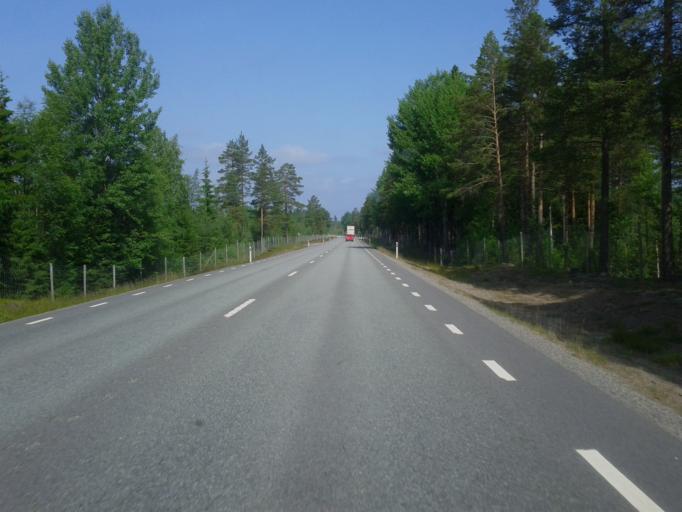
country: SE
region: Vaesterbotten
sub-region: Skelleftea Kommun
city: Burea
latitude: 64.5817
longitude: 21.2206
